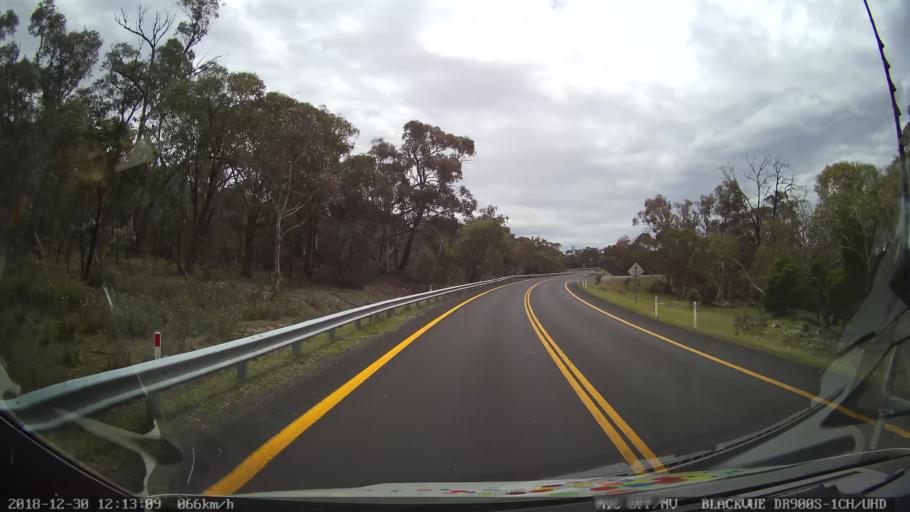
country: AU
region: New South Wales
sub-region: Snowy River
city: Jindabyne
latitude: -36.3510
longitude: 148.5855
